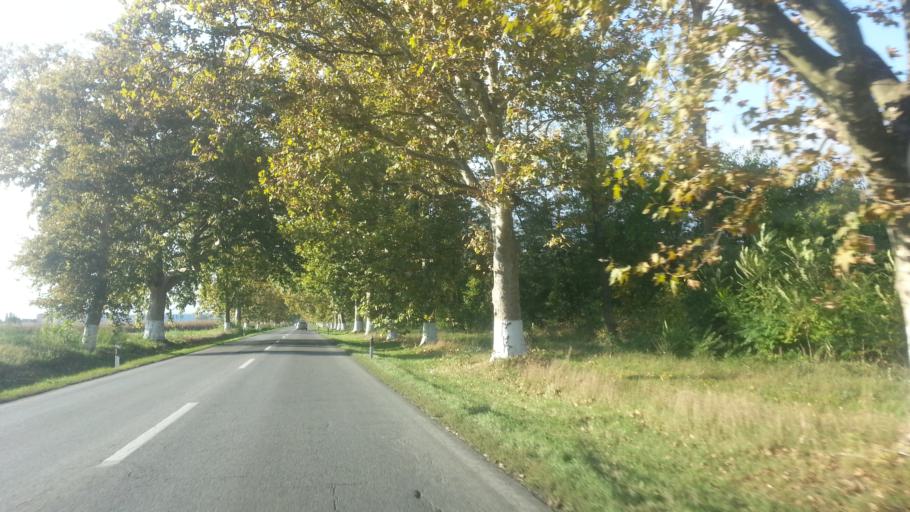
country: RS
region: Autonomna Pokrajina Vojvodina
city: Nova Pazova
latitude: 44.9318
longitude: 20.2377
